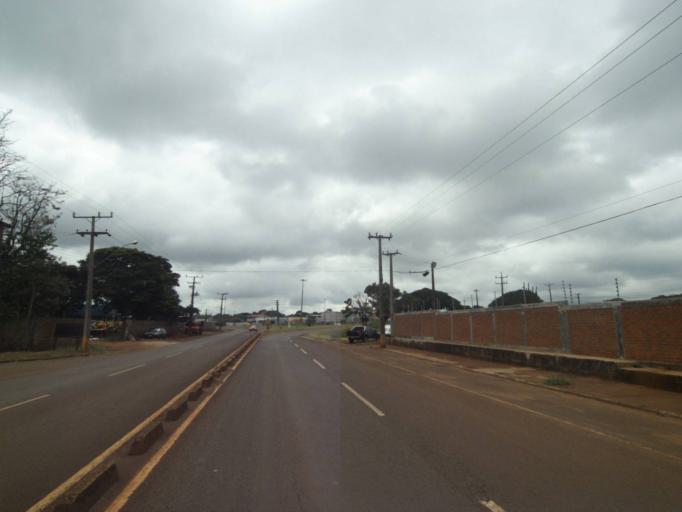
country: BR
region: Parana
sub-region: Campo Mourao
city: Campo Mourao
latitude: -24.0208
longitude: -52.3651
